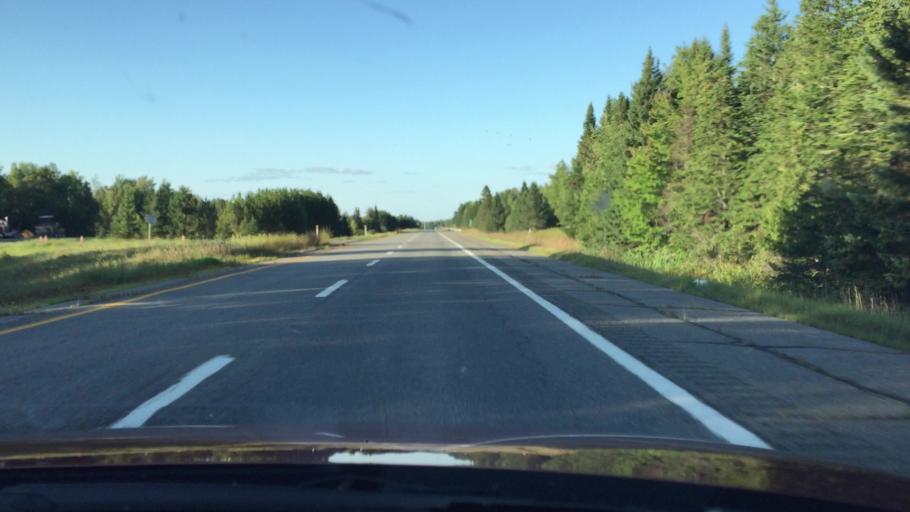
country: US
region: Maine
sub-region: Penobscot County
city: Patten
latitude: 45.8560
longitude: -68.4235
